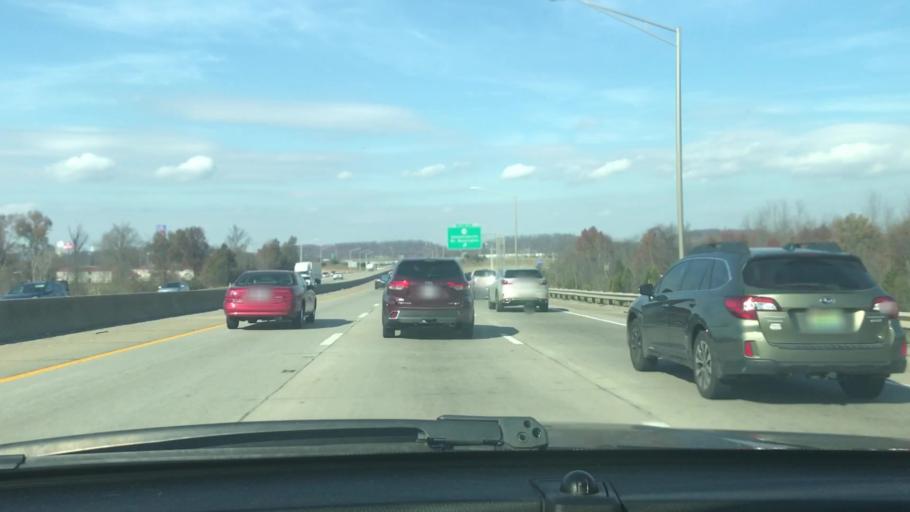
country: US
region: Kentucky
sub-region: Bullitt County
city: Shepherdsville
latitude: 37.9872
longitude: -85.7016
